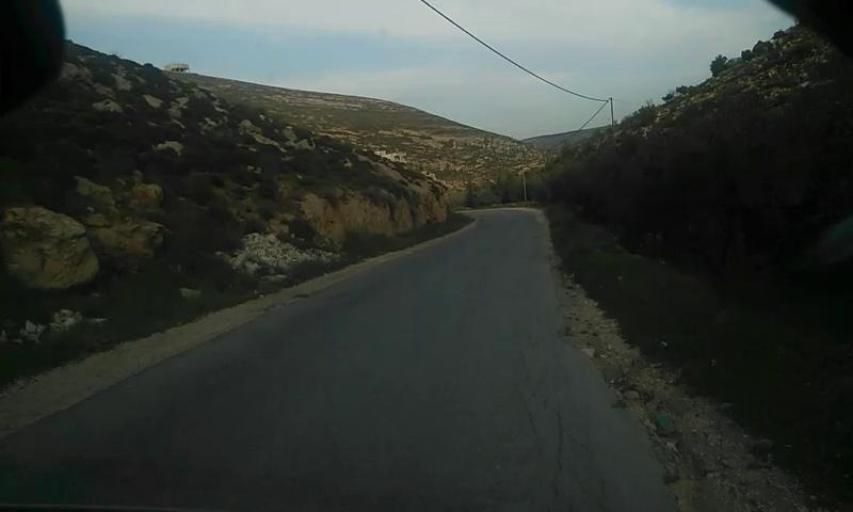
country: PS
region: West Bank
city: Ash Shuyukh
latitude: 31.5926
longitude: 35.1622
